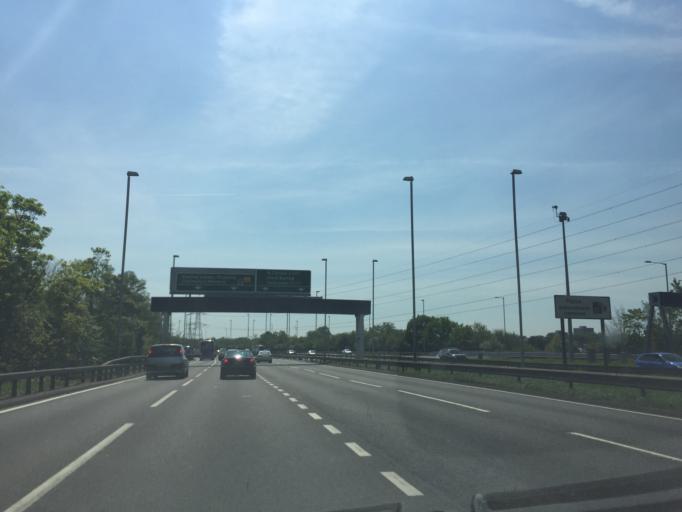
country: GB
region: England
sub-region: Greater London
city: Woodford Green
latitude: 51.5852
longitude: 0.0403
